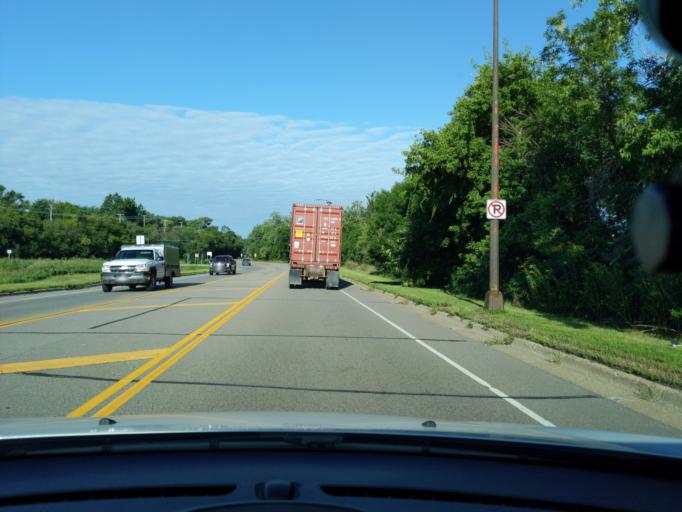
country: US
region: Minnesota
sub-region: Ramsey County
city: Falcon Heights
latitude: 44.9694
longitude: -93.1682
